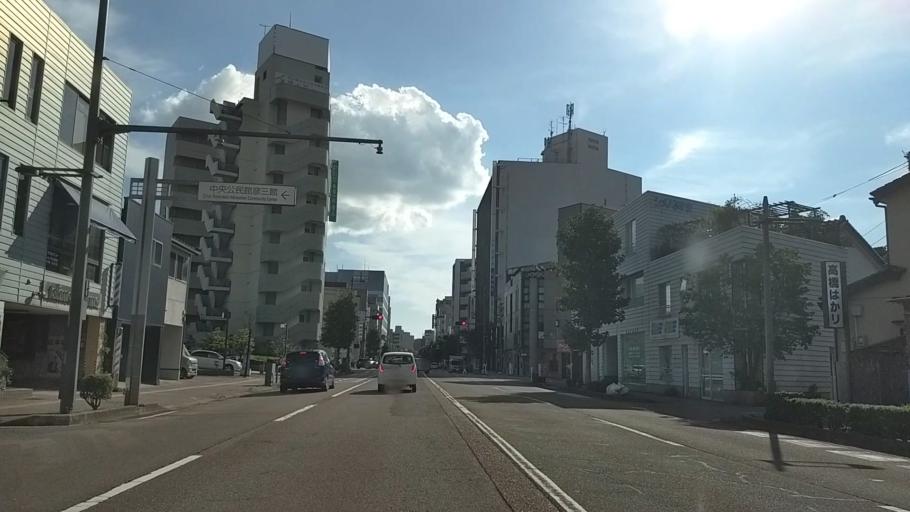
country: JP
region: Ishikawa
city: Kanazawa-shi
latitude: 36.5756
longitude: 136.6596
